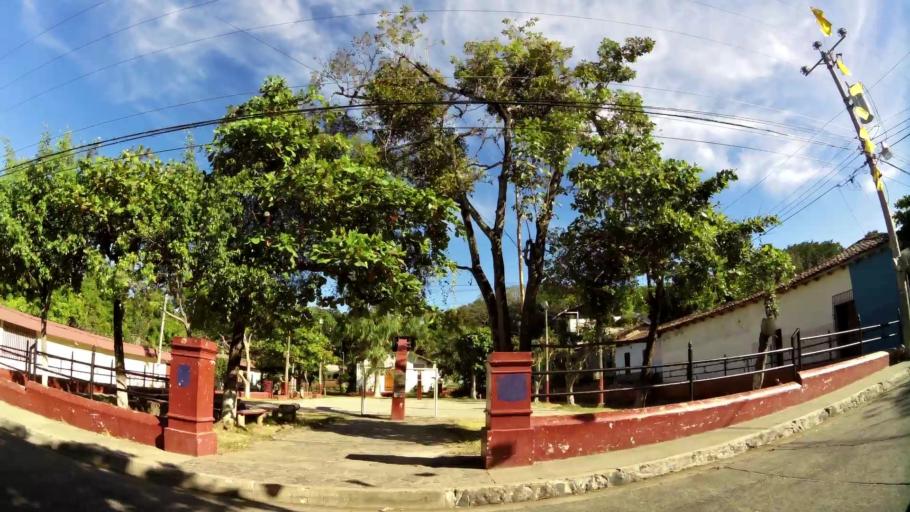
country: SV
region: Cuscatlan
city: Suchitoto
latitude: 13.9300
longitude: -89.0303
